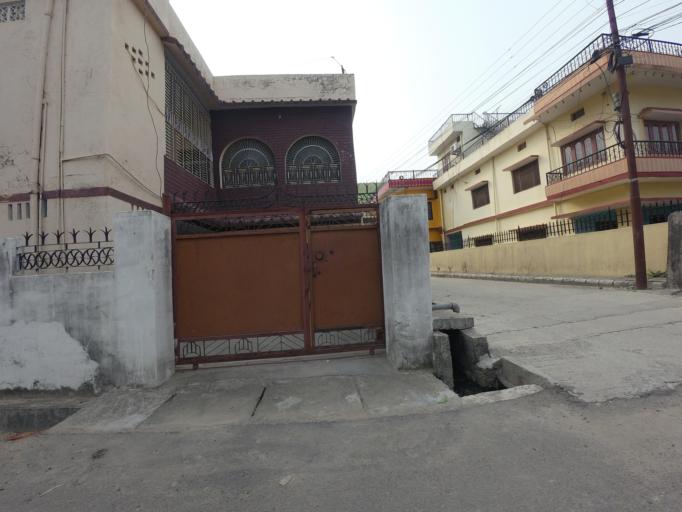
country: NP
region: Western Region
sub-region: Lumbini Zone
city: Bhairahawa
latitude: 27.5220
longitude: 83.4517
